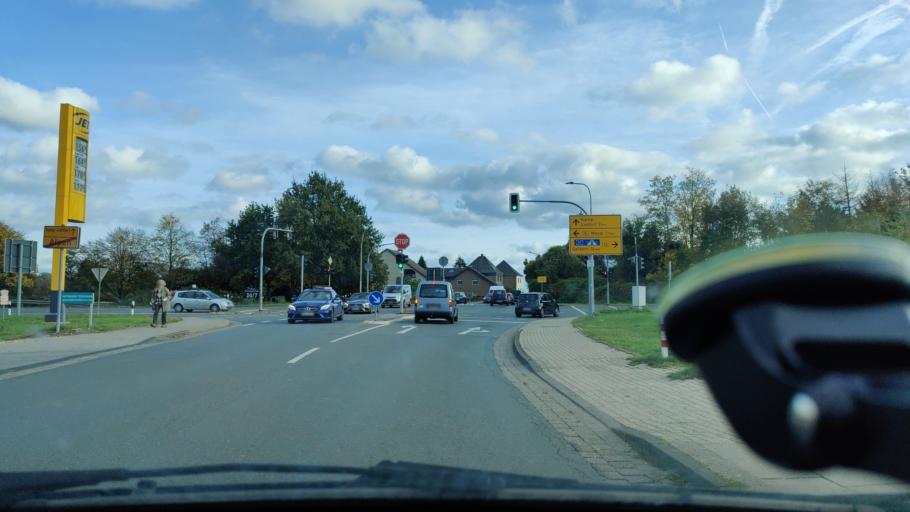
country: DE
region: North Rhine-Westphalia
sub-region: Regierungsbezirk Dusseldorf
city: Alpen
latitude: 51.5717
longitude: 6.5217
